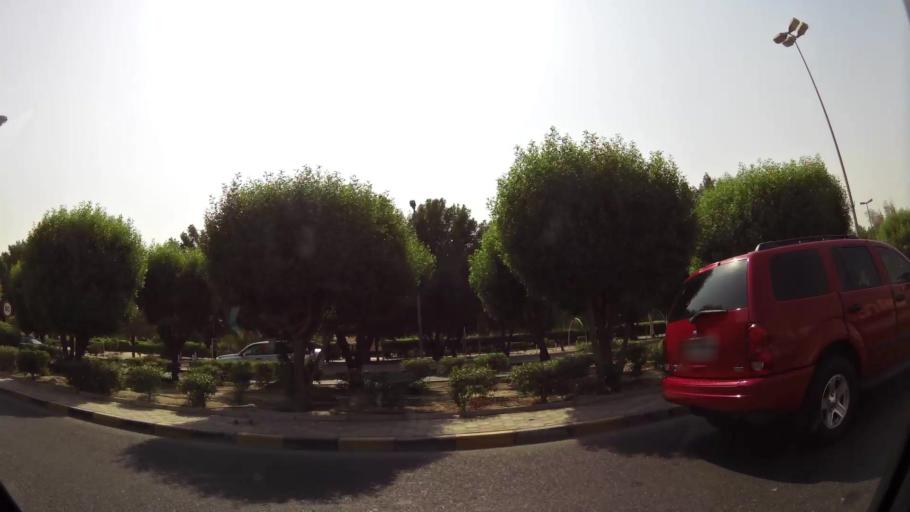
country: KW
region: Al Asimah
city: Ash Shamiyah
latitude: 29.3338
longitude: 47.9566
